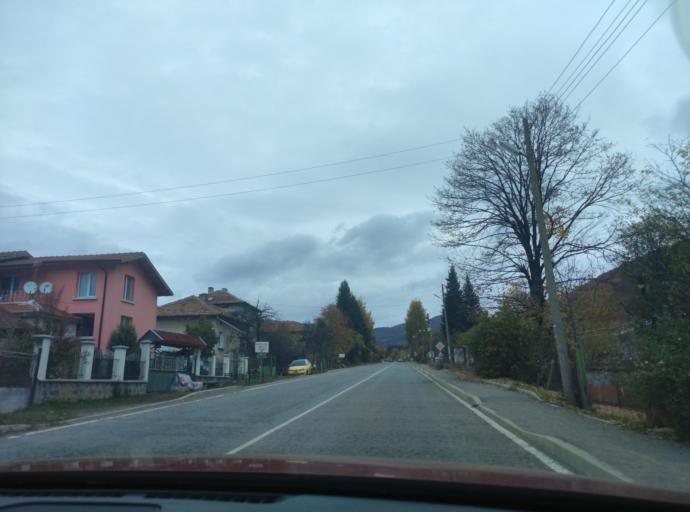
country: BG
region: Sofiya
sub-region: Obshtina Godech
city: Godech
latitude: 43.0941
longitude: 23.0992
